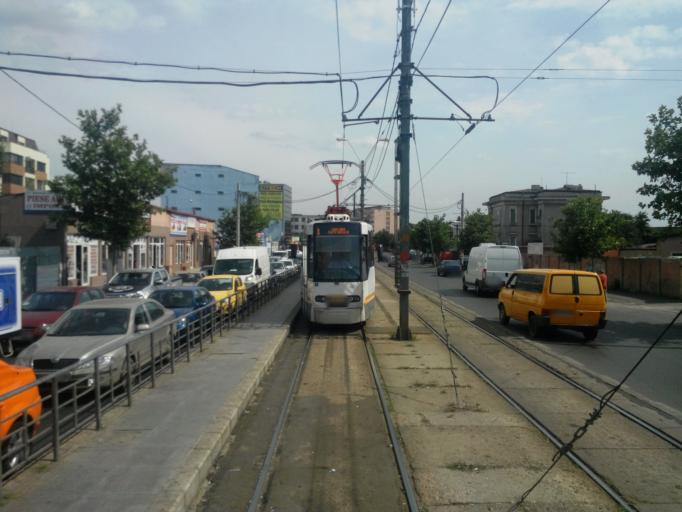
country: RO
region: Bucuresti
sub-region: Municipiul Bucuresti
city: Bucuresti
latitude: 44.4109
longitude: 26.0892
